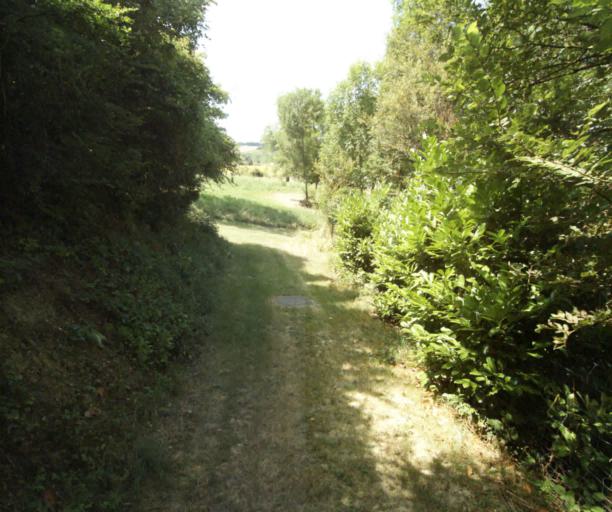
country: FR
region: Midi-Pyrenees
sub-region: Departement de la Haute-Garonne
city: Saint-Felix-Lauragais
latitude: 43.4503
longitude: 1.8883
